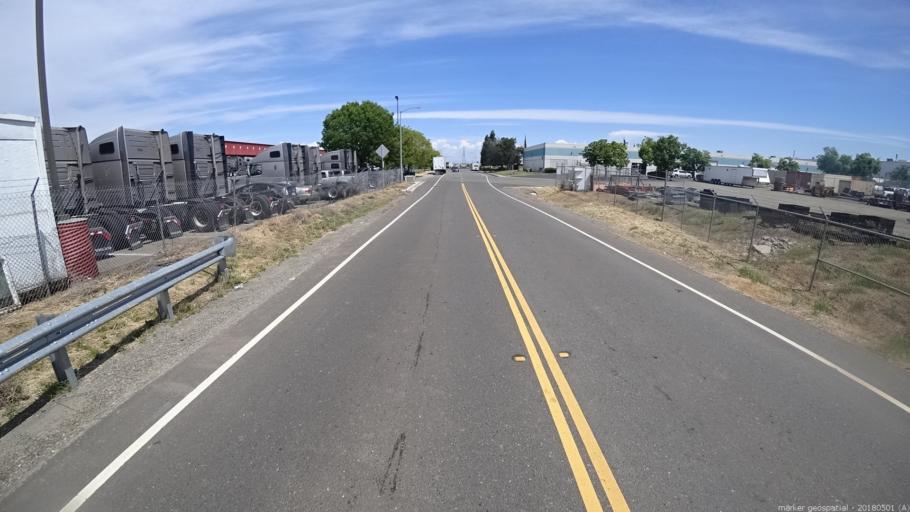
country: US
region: California
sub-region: Sacramento County
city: Rio Linda
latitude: 38.6655
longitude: -121.4312
